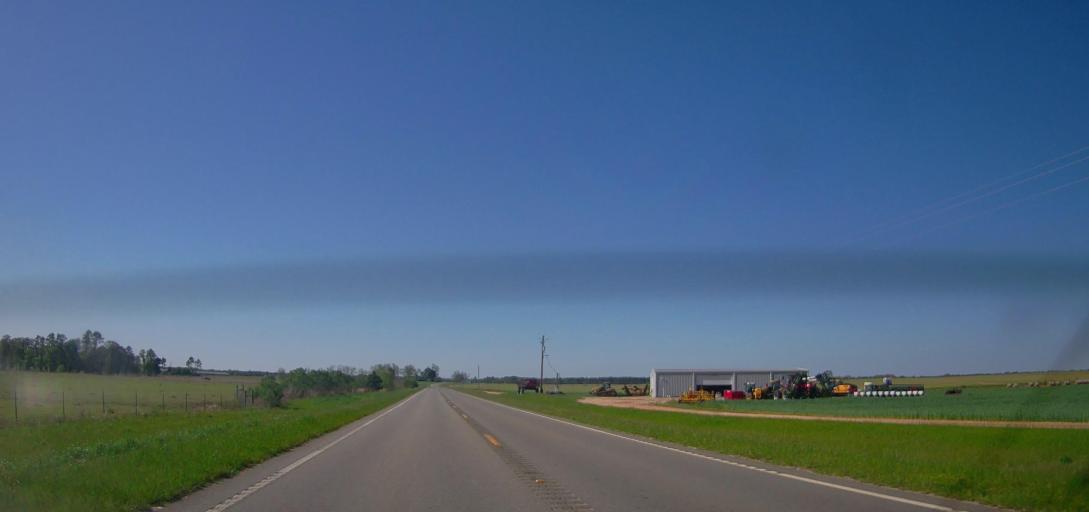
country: US
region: Georgia
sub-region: Pulaski County
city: Hawkinsville
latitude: 32.1377
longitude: -83.5082
